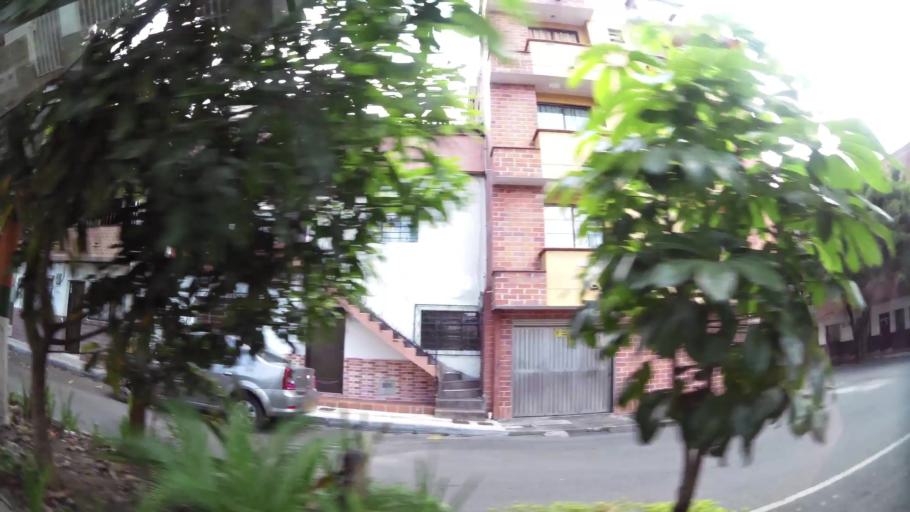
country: CO
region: Antioquia
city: Envigado
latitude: 6.1751
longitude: -75.5816
